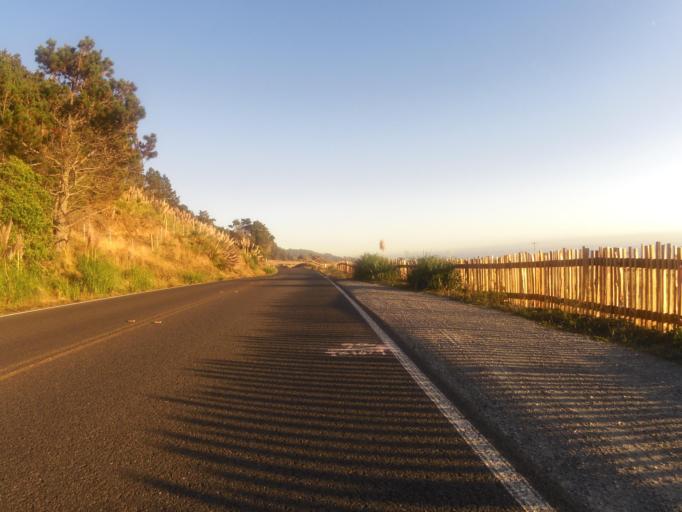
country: US
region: California
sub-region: Sonoma County
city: Sea Ranch
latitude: 38.6677
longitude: -123.4109
